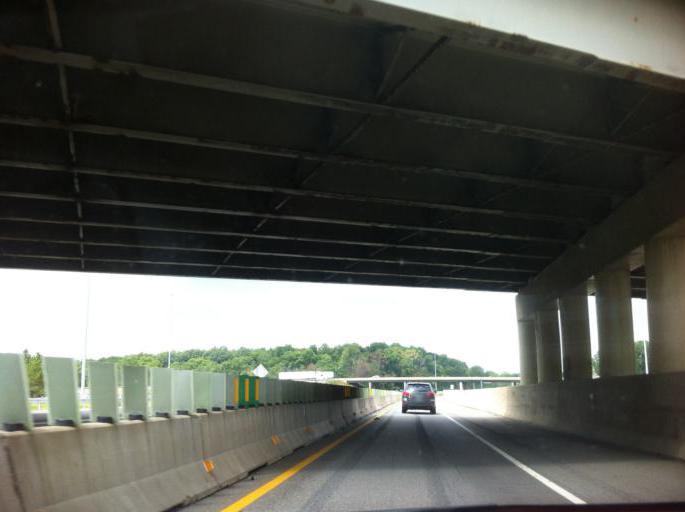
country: US
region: Ohio
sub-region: Cuyahoga County
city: Strongsville
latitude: 41.3327
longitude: -81.8165
